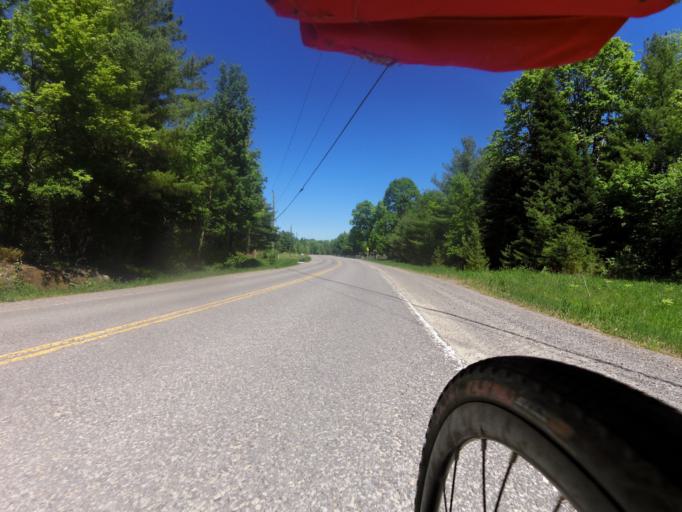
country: CA
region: Ontario
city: Carleton Place
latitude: 45.1862
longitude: -76.3395
